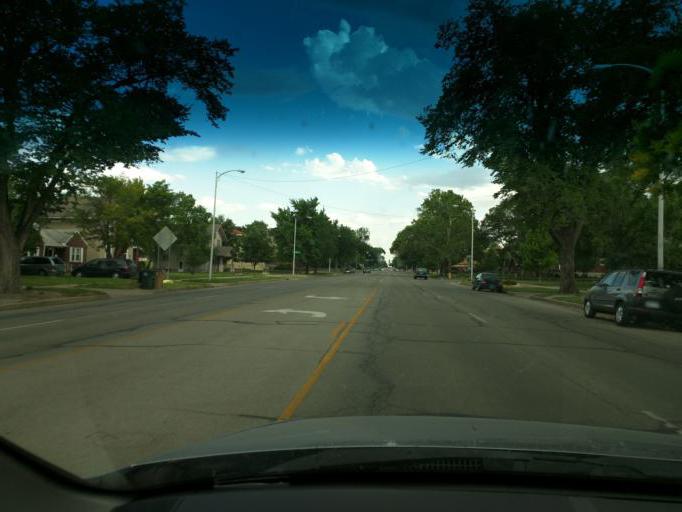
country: US
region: Kansas
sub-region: Reno County
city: Hutchinson
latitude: 38.0748
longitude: -97.9319
